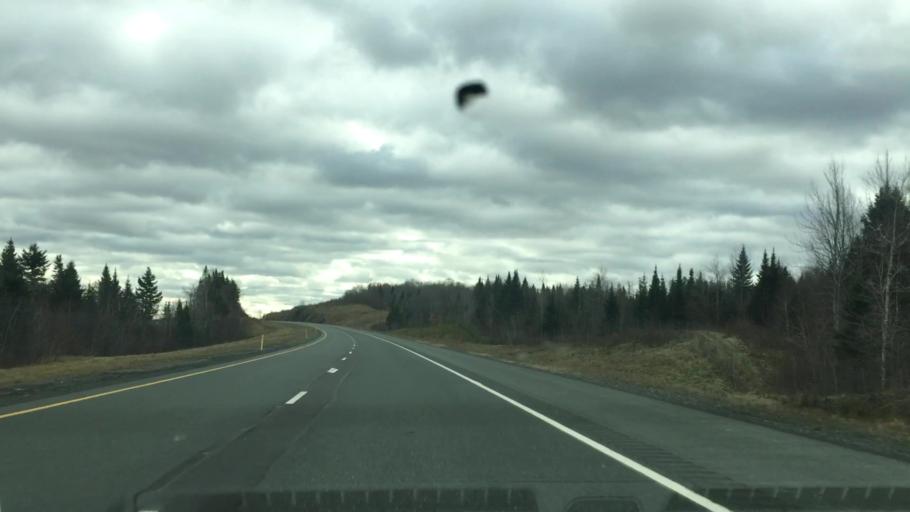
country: US
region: Maine
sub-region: Aroostook County
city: Fort Fairfield
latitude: 46.6398
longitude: -67.7444
